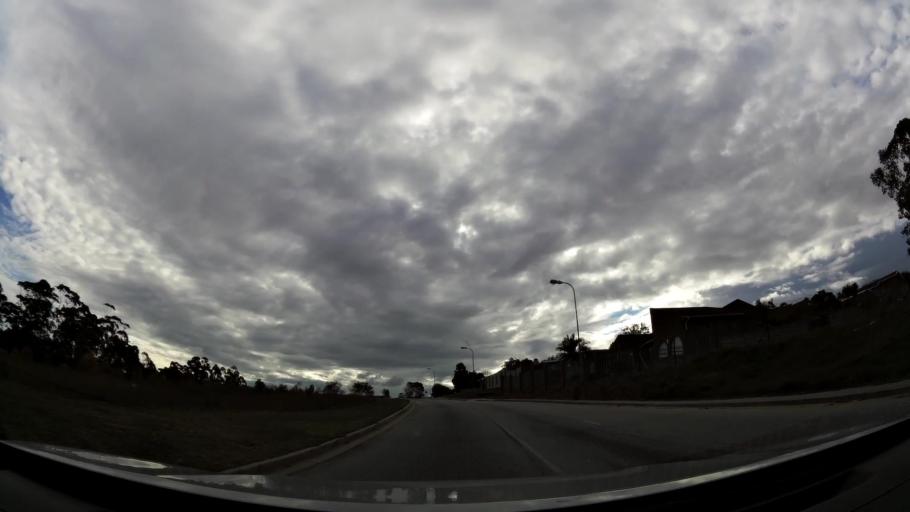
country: ZA
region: Eastern Cape
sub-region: Nelson Mandela Bay Metropolitan Municipality
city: Port Elizabeth
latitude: -33.9531
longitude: 25.5074
